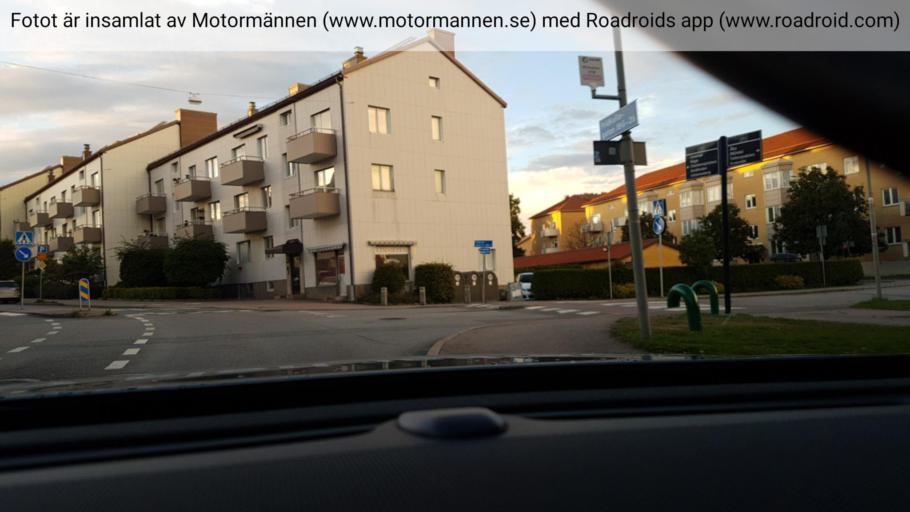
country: SE
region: Vaestra Goetaland
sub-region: Goteborg
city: Goeteborg
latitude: 57.6823
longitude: 11.9877
